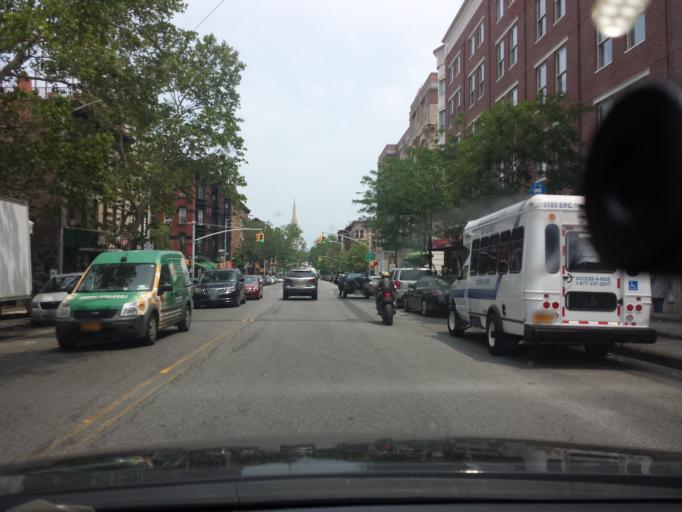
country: US
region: New York
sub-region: Kings County
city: Brooklyn
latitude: 40.6688
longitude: -73.9800
